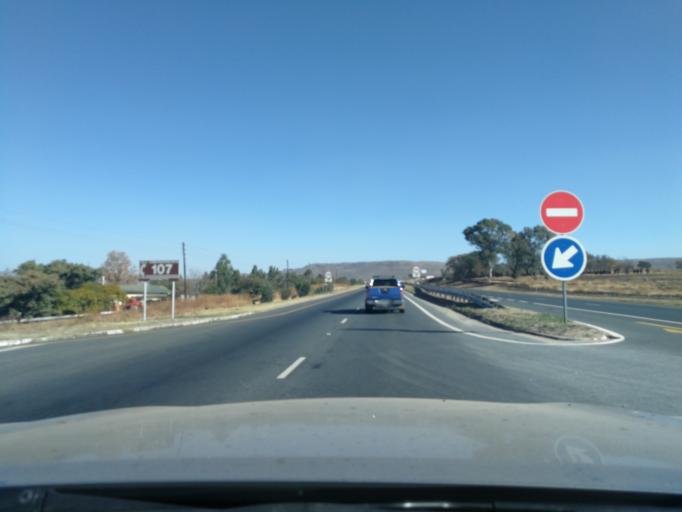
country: ZA
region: Gauteng
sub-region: West Rand District Municipality
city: Muldersdriseloop
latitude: -26.0463
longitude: 27.8411
